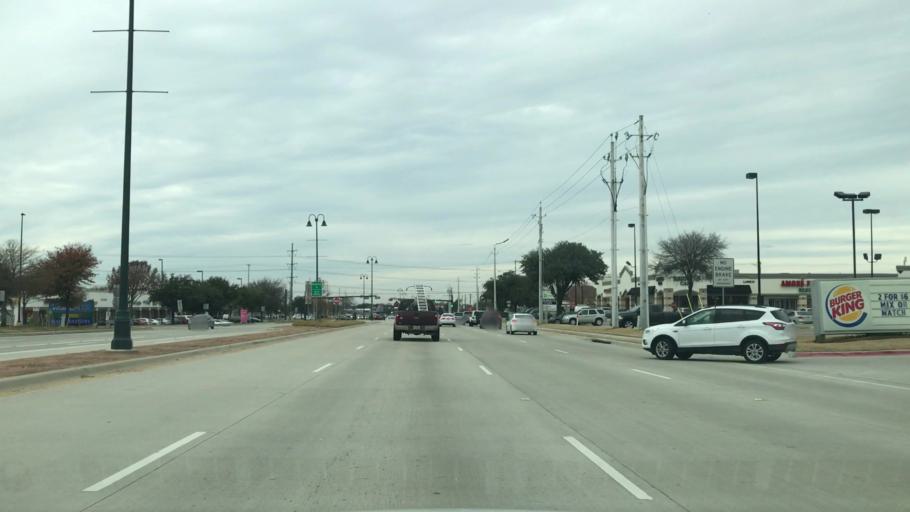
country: US
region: Texas
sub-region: Denton County
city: The Colony
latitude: 33.0670
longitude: -96.8896
